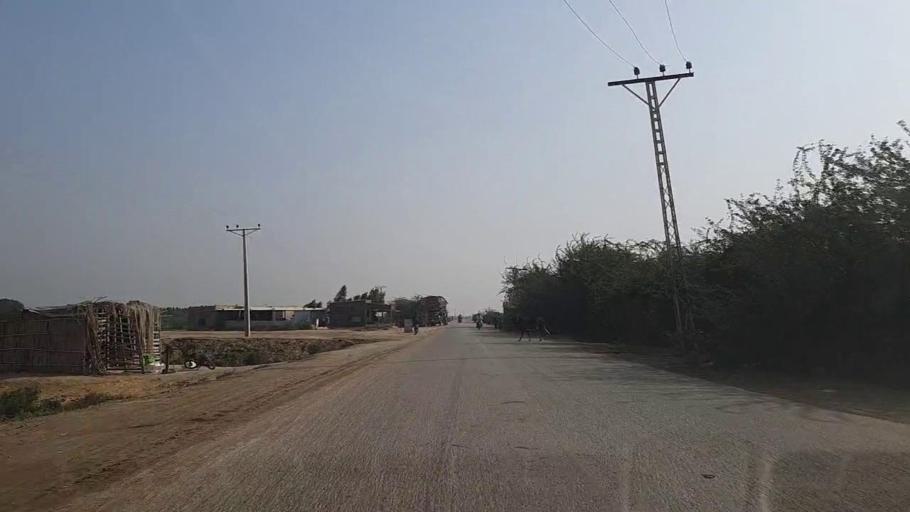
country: PK
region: Sindh
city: Keti Bandar
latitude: 24.2308
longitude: 67.6093
